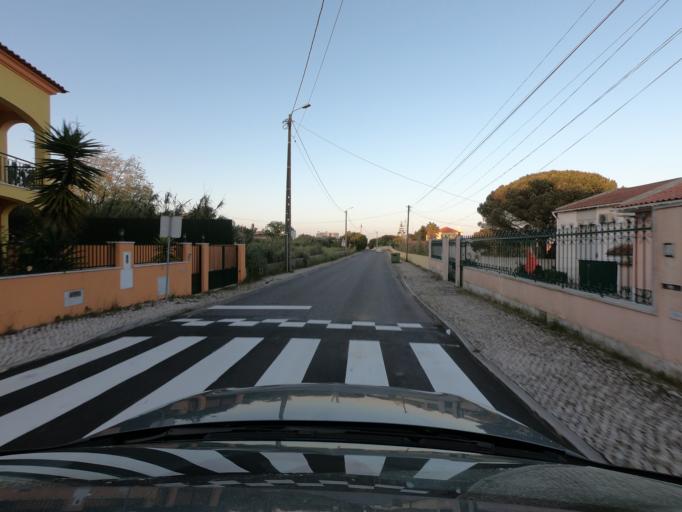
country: PT
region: Lisbon
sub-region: Sintra
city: Rio de Mouro
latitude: 38.7586
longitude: -9.3558
